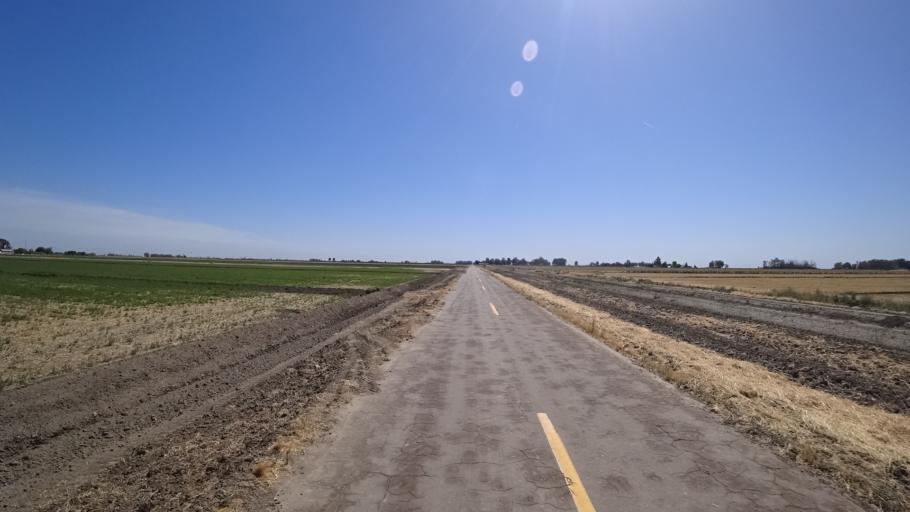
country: US
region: California
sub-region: Kings County
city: Stratford
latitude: 36.2041
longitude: -119.8085
